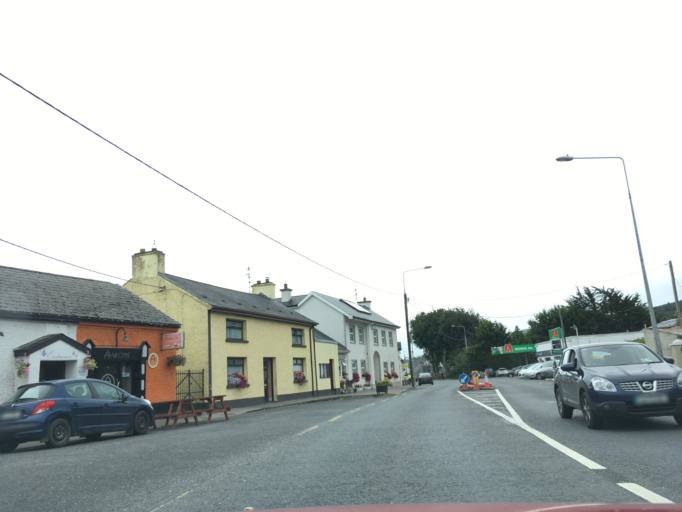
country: IE
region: Munster
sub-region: South Tipperary
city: Cluain Meala
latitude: 52.3612
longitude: -7.5799
